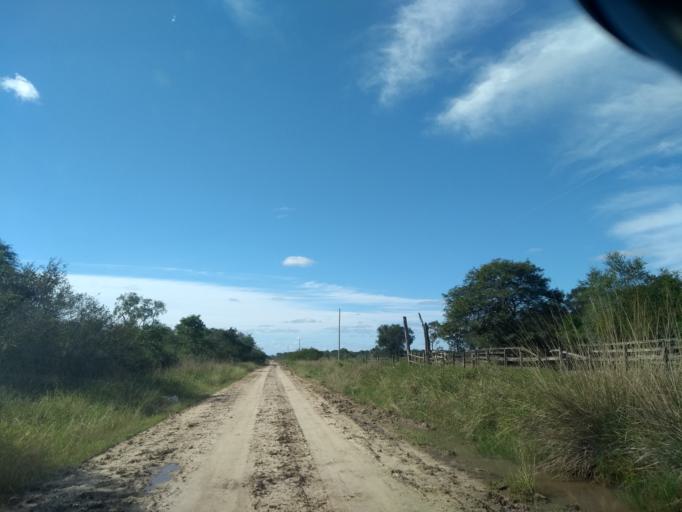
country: AR
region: Chaco
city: Colonia Benitez
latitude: -27.2910
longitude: -58.9357
